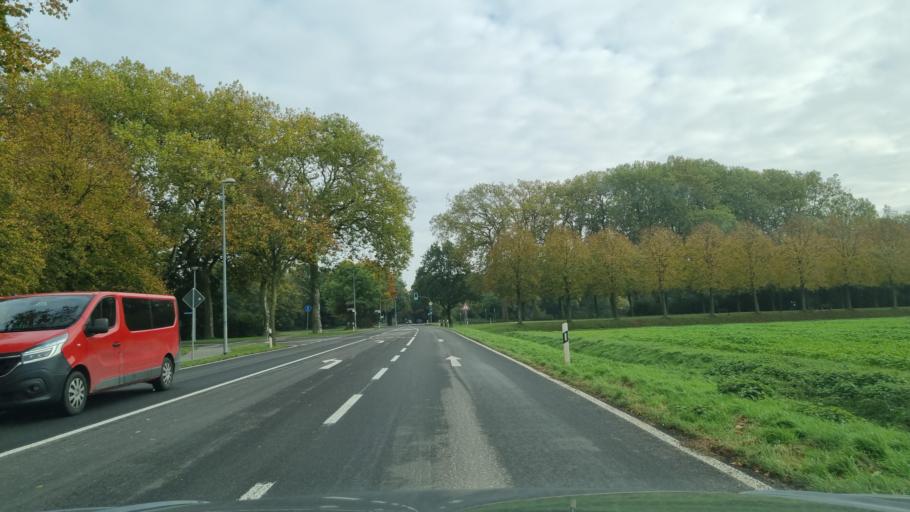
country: DE
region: North Rhine-Westphalia
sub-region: Regierungsbezirk Dusseldorf
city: Kleve
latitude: 51.8022
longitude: 6.1266
